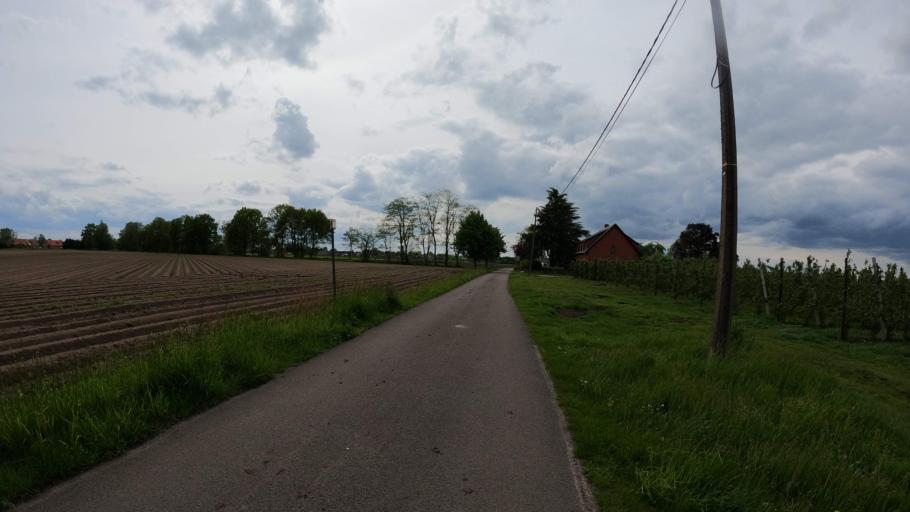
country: BE
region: Flanders
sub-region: Provincie Antwerpen
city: Oud-Turnhout
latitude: 51.3098
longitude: 4.9753
